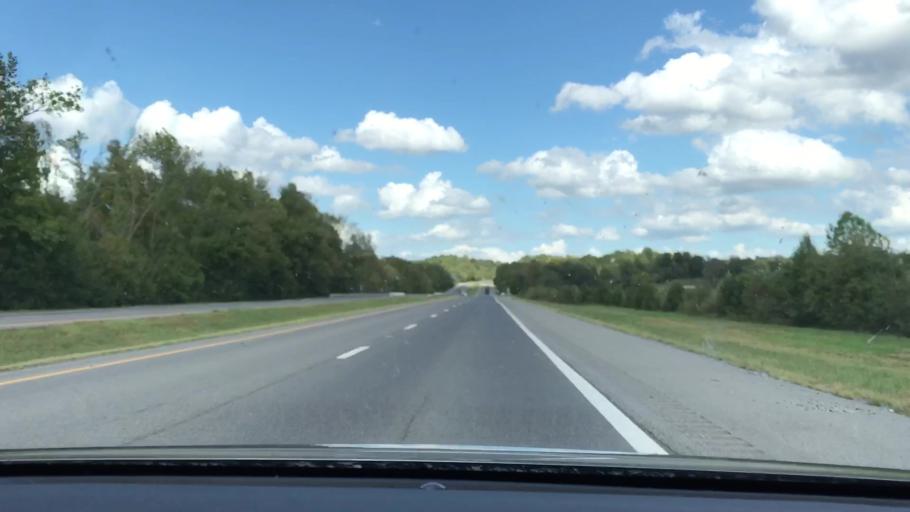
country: US
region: Kentucky
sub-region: Marshall County
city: Benton
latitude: 36.8091
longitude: -88.4914
